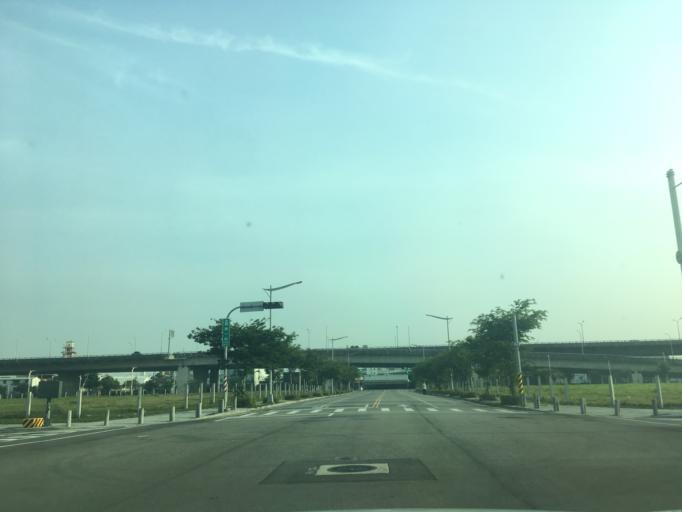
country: TW
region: Taiwan
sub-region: Taichung City
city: Taichung
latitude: 24.1992
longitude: 120.6805
